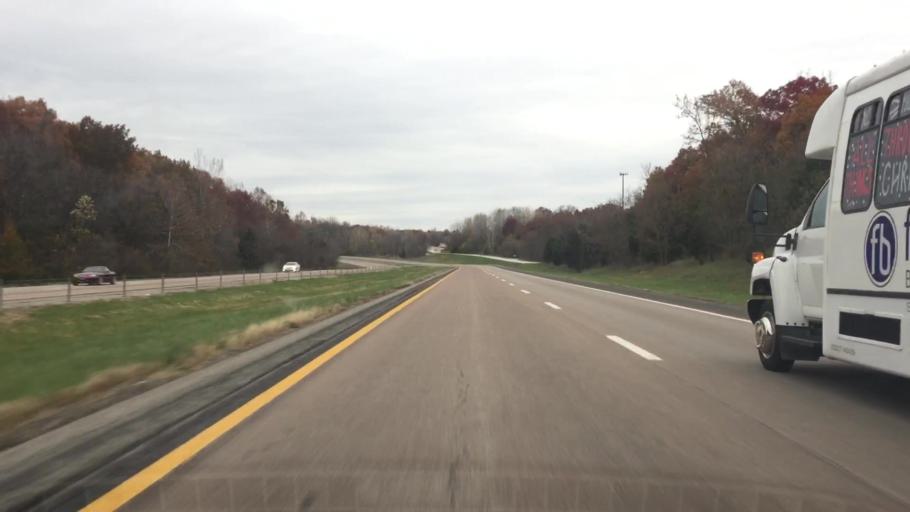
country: US
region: Missouri
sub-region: Cole County
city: Jefferson City
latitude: 38.6649
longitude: -92.2269
